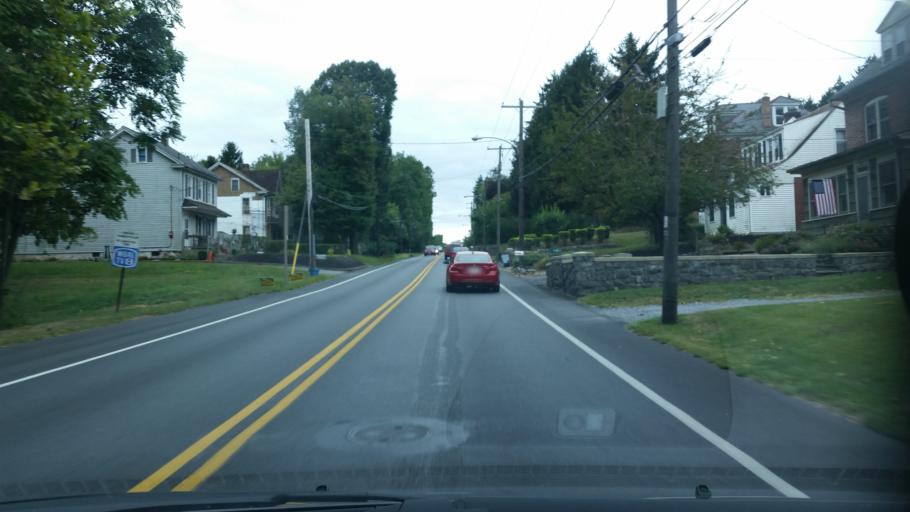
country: US
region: Pennsylvania
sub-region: Lancaster County
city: Lancaster
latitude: 40.0174
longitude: -76.3018
